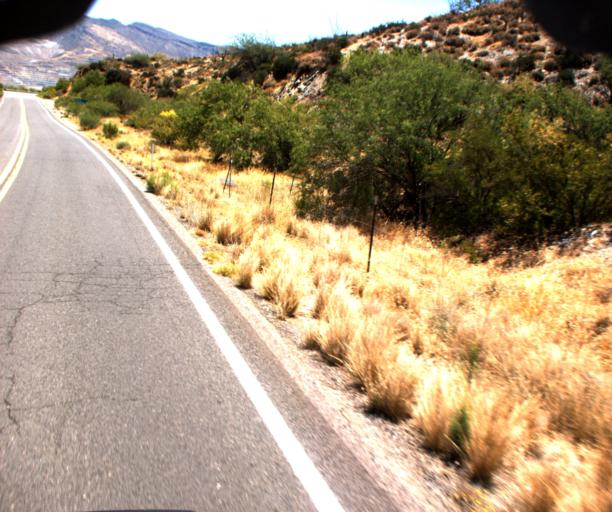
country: US
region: Arizona
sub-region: Pinal County
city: Superior
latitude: 33.1749
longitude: -111.0313
